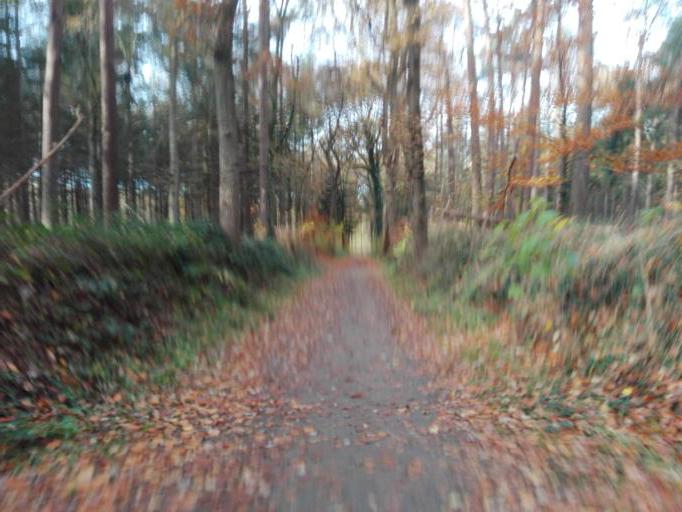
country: DE
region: Lower Saxony
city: Rastede
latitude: 53.2738
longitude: 8.1619
